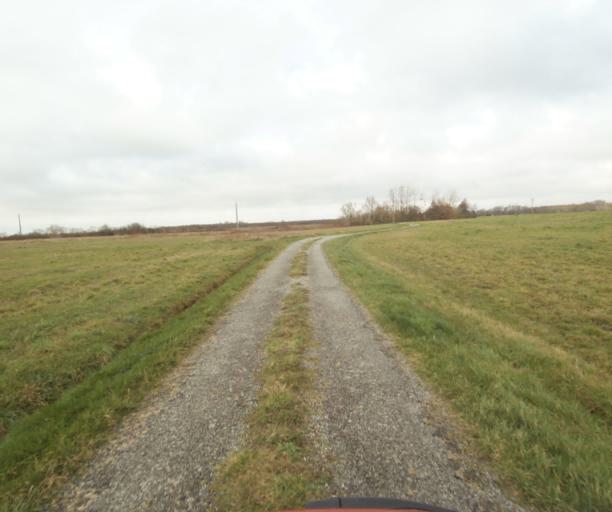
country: FR
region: Midi-Pyrenees
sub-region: Departement de l'Ariege
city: La Tour-du-Crieu
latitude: 43.1568
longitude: 1.6915
